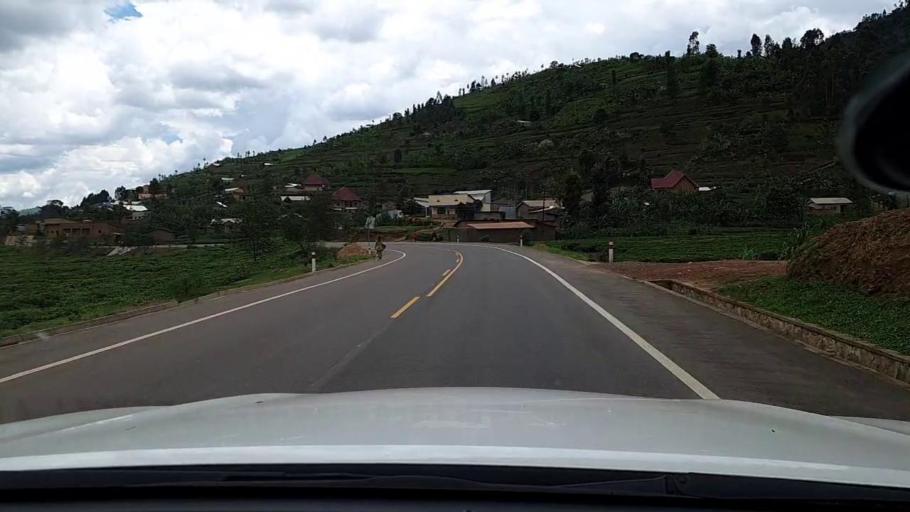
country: RW
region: Northern Province
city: Byumba
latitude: -1.6525
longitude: 29.9034
